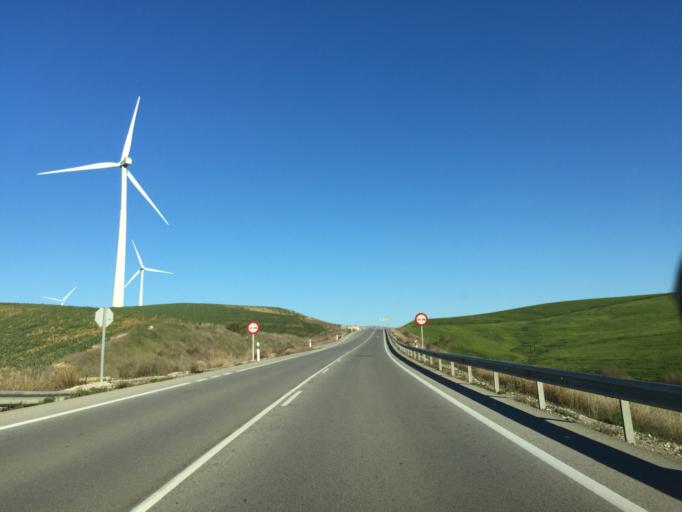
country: ES
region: Andalusia
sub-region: Provincia de Malaga
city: Ardales
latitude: 36.9336
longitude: -4.8614
